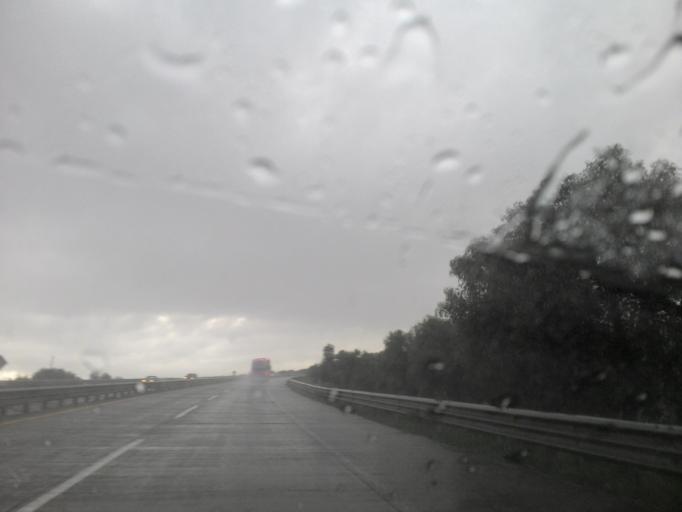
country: MX
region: Hidalgo
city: Zempoala
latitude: 19.8835
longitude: -98.6564
